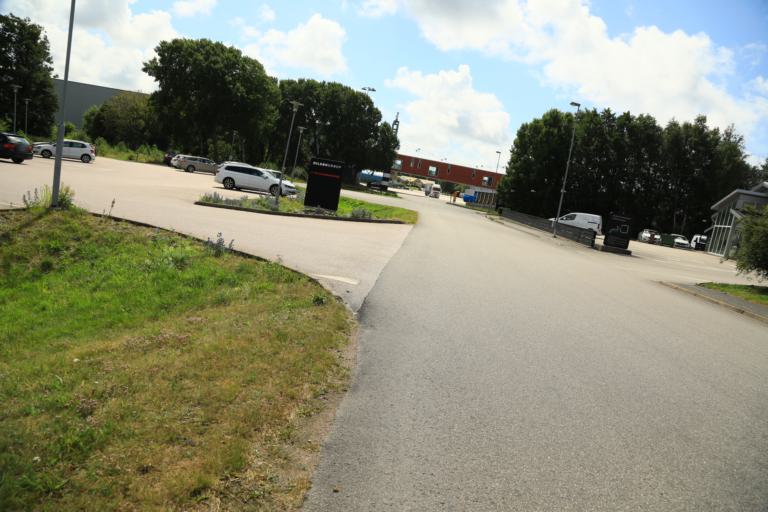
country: SE
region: Halland
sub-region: Varbergs Kommun
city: Varberg
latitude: 57.1189
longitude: 12.2923
